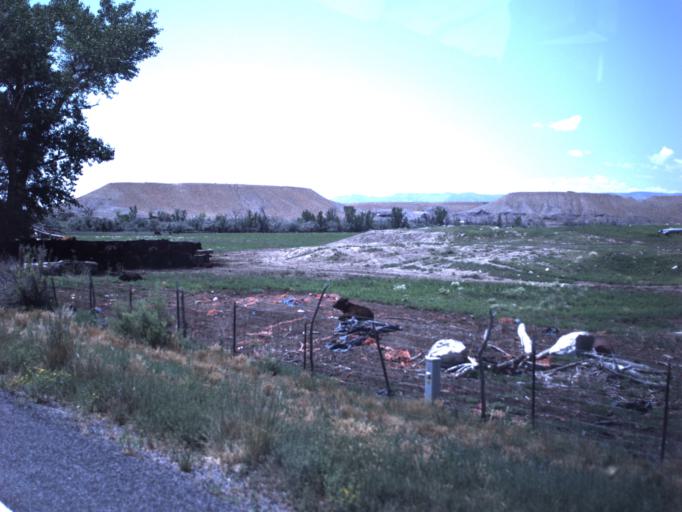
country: US
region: Utah
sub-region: Emery County
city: Castle Dale
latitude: 39.1900
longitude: -111.0477
